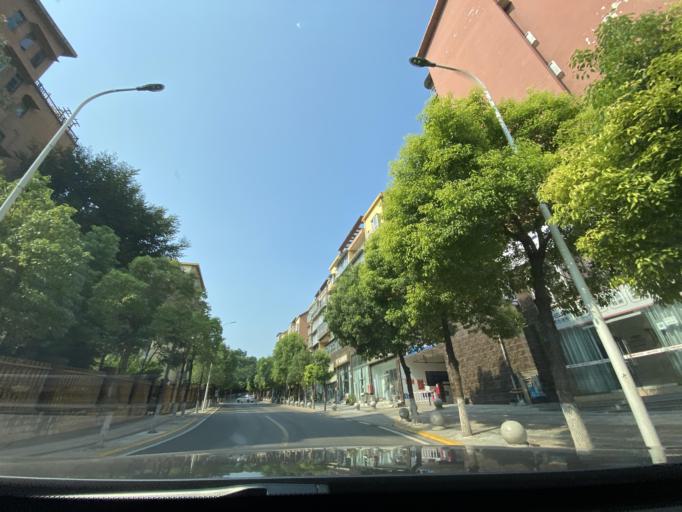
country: CN
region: Sichuan
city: Jiancheng
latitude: 30.4174
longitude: 104.5440
